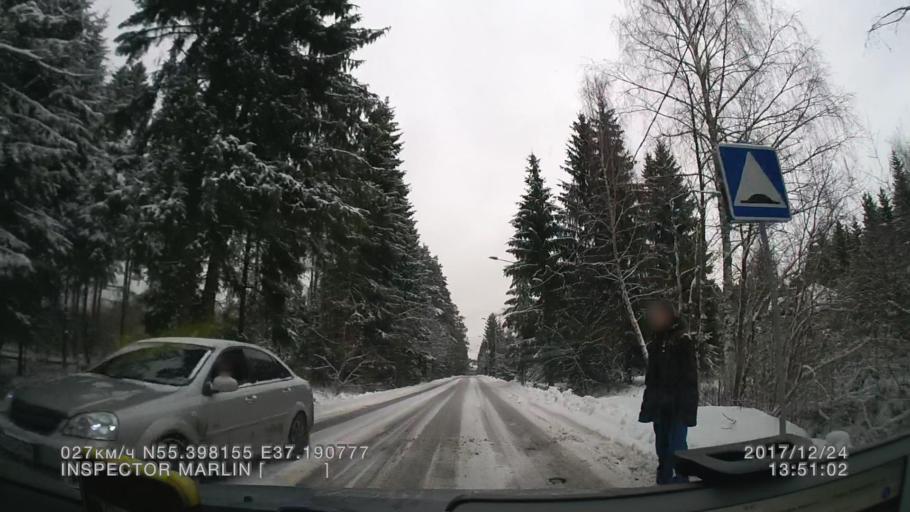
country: RU
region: Moskovskaya
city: Troitsk
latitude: 55.3982
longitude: 37.1908
